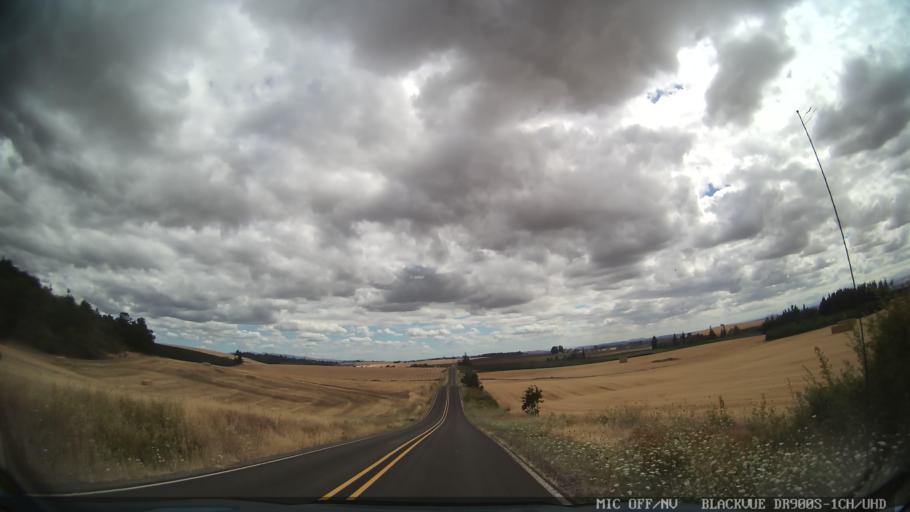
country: US
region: Oregon
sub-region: Marion County
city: Sublimity
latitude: 44.8638
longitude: -122.7386
